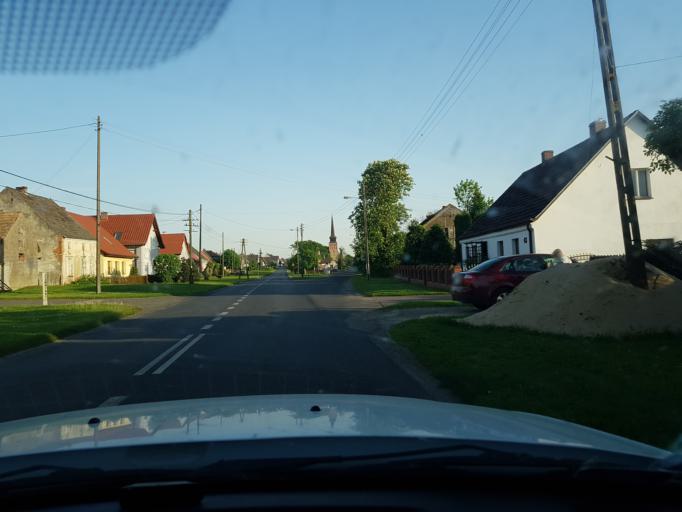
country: PL
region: West Pomeranian Voivodeship
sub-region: Powiat goleniowski
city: Mosty
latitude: 53.4648
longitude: 14.9289
